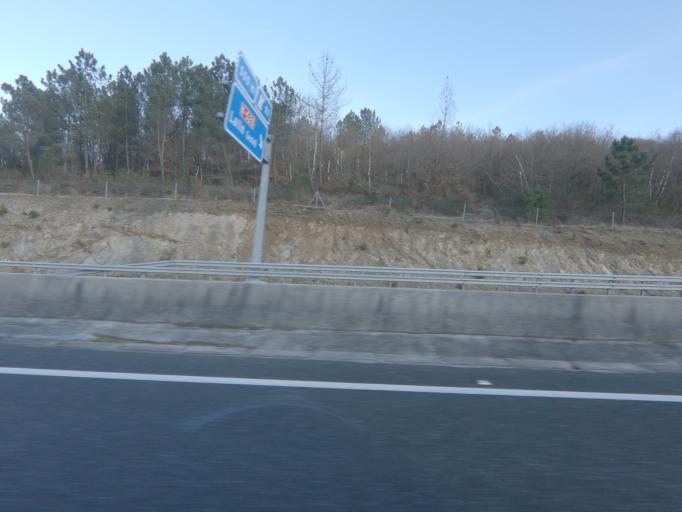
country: ES
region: Galicia
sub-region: Provincia de Pontevedra
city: Lalin
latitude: 42.6118
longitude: -8.1004
